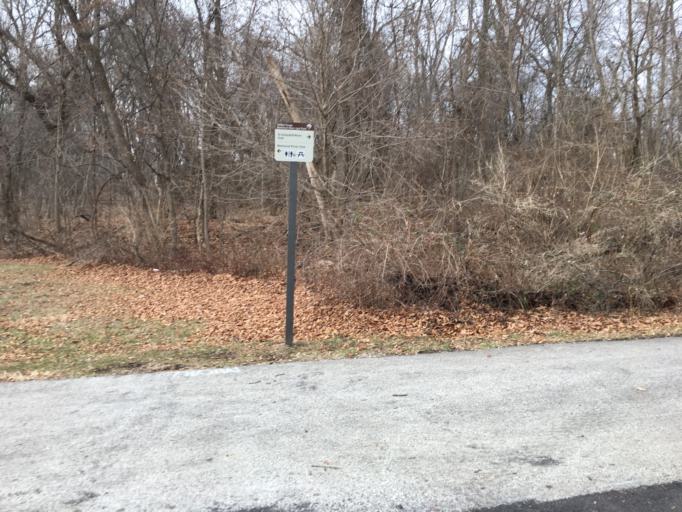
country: US
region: Pennsylvania
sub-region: Montgomery County
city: Audubon
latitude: 40.1099
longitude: -75.4211
